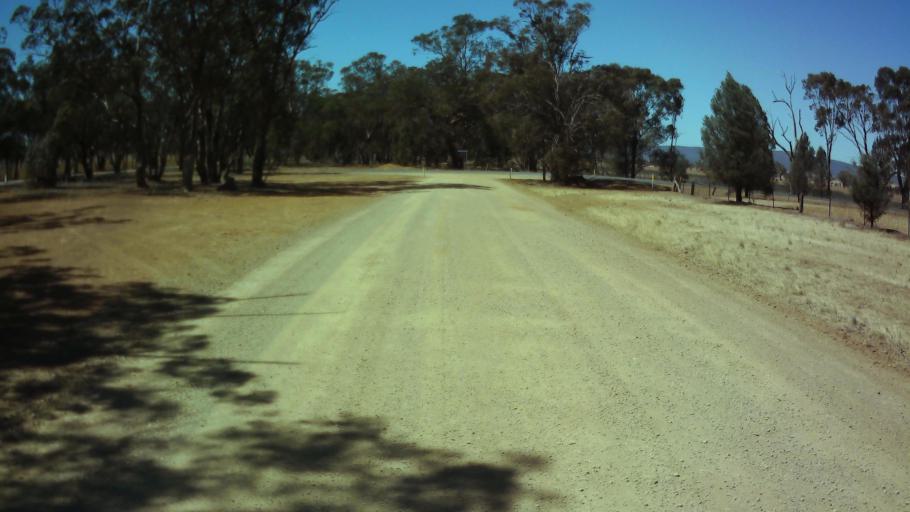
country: AU
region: New South Wales
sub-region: Weddin
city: Grenfell
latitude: -33.8696
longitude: 148.0878
